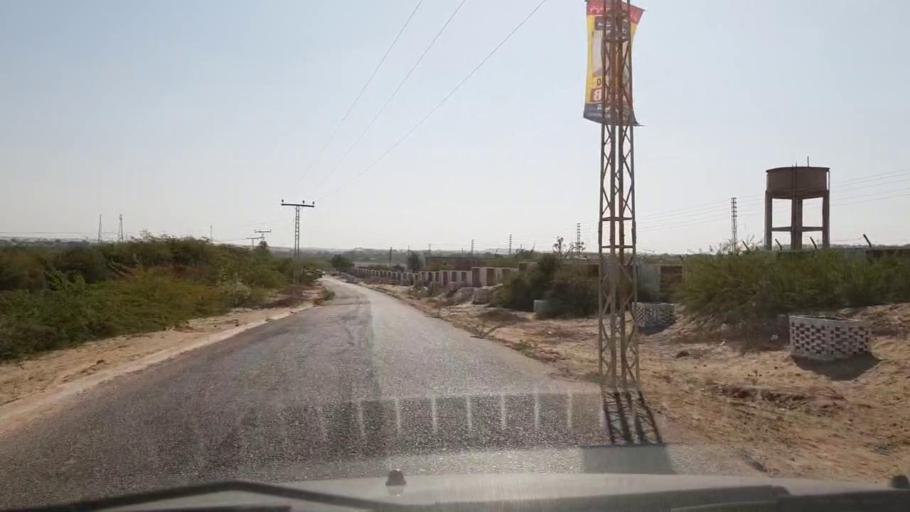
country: PK
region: Sindh
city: Diplo
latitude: 24.4786
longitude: 69.5807
